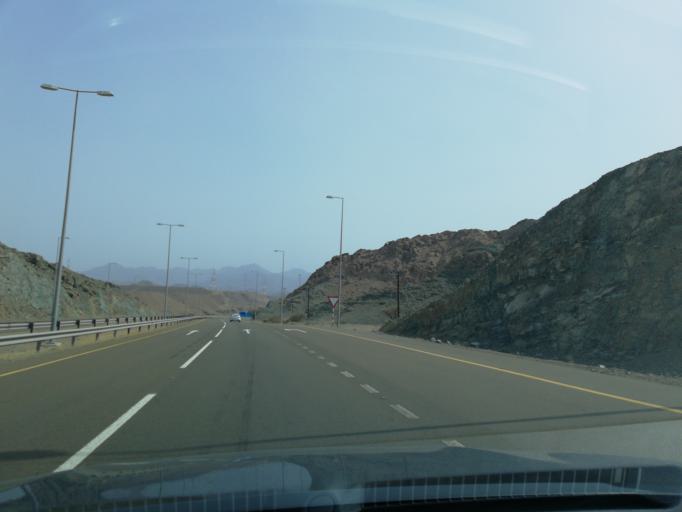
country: OM
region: Al Batinah
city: Al Liwa'
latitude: 24.3000
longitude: 56.4253
